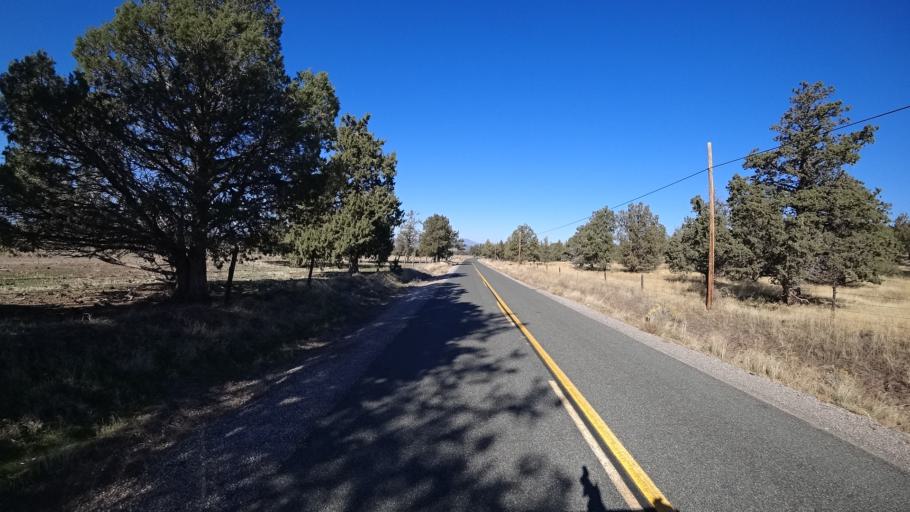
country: US
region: California
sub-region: Siskiyou County
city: Weed
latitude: 41.6272
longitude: -122.3308
